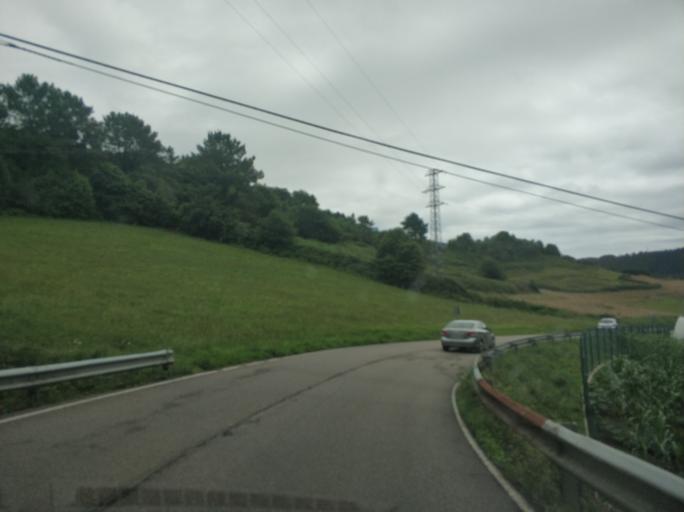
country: ES
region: Asturias
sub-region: Province of Asturias
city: Cudillero
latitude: 43.5649
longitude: -6.2379
